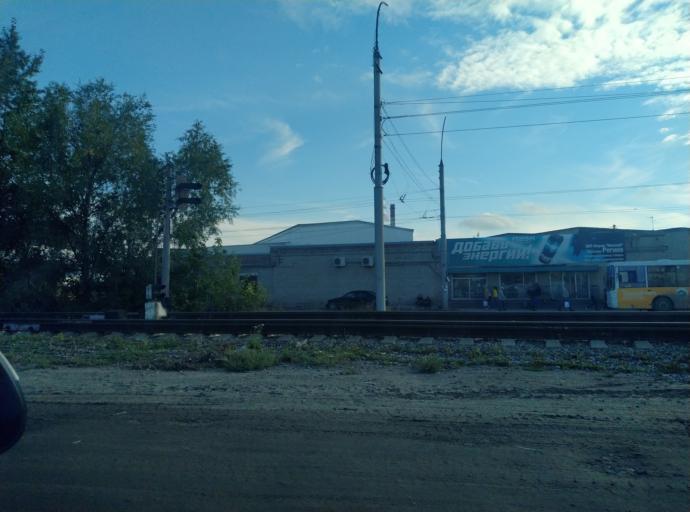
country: RU
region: Novosibirsk
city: Tolmachevo
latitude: 55.0136
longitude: 82.8093
